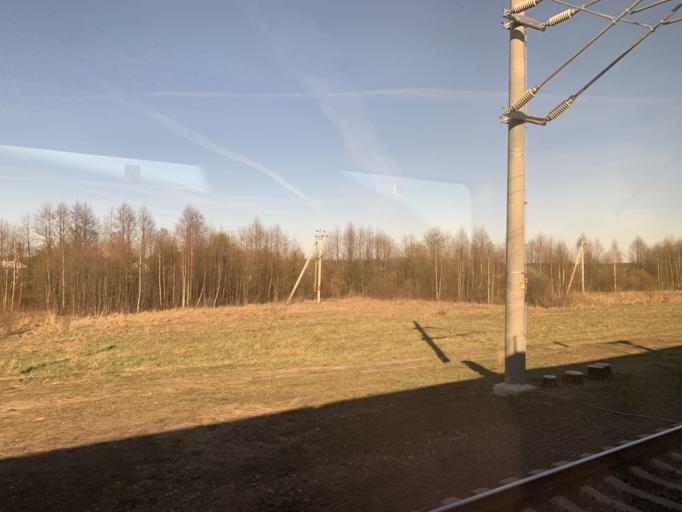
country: BY
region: Minsk
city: Turets-Bayary
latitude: 54.4182
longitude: 26.5464
